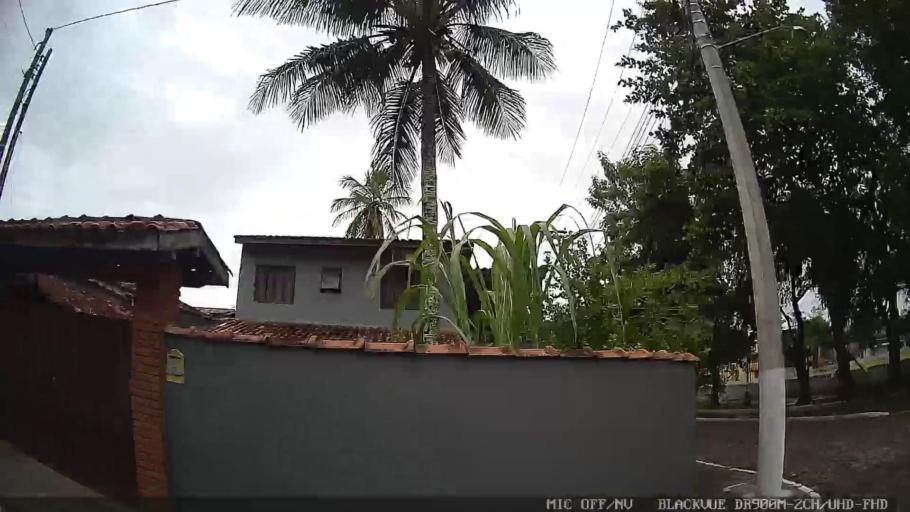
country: BR
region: Sao Paulo
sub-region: Sao Sebastiao
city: Sao Sebastiao
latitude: -23.7274
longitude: -45.4233
